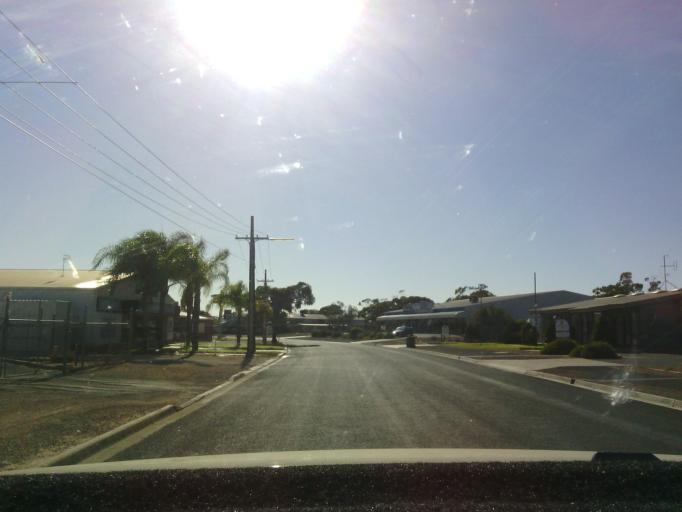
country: AU
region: South Australia
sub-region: Berri and Barmera
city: Berri
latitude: -34.2714
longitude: 140.6011
